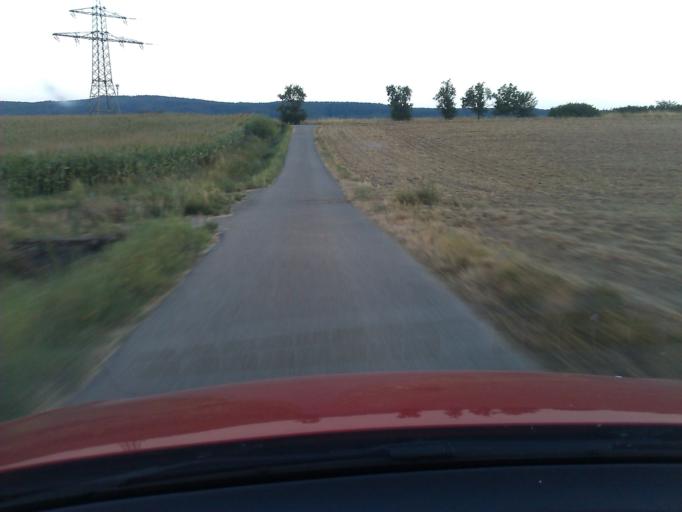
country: DE
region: Baden-Wuerttemberg
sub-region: Regierungsbezirk Stuttgart
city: Pfaffenhofen
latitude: 49.0693
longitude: 8.9857
